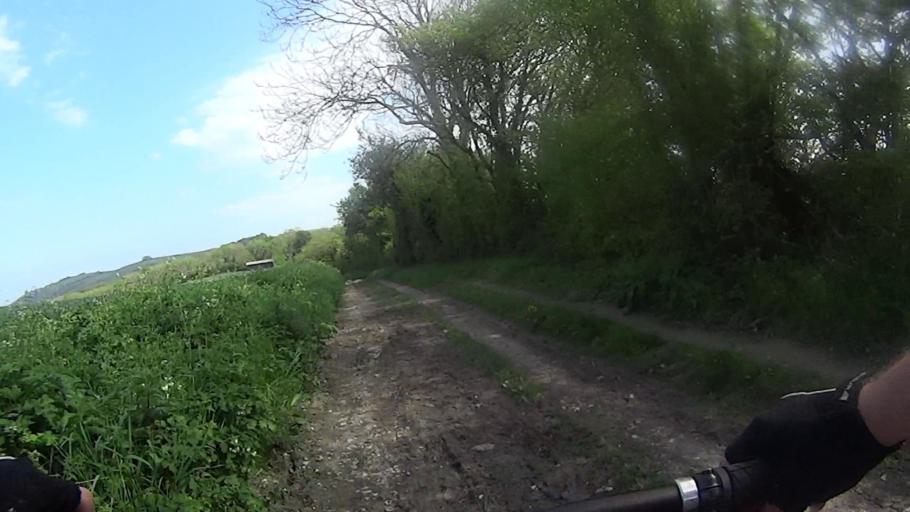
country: GB
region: England
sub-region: Hampshire
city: Petersfield
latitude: 50.9645
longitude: -0.8995
